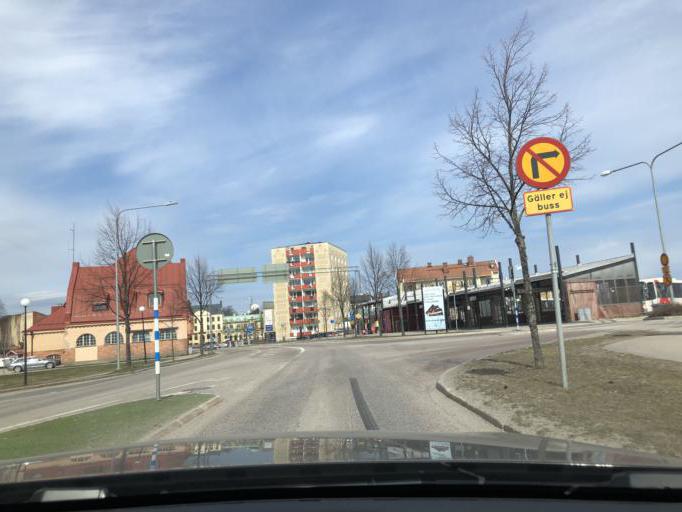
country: SE
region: Gaevleborg
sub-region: Hudiksvalls Kommun
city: Hudiksvall
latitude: 61.7247
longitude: 17.1077
